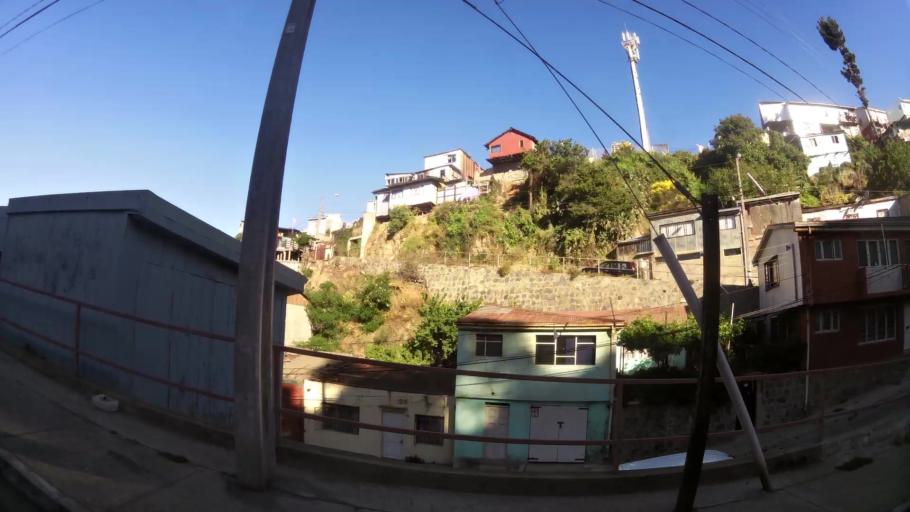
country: CL
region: Valparaiso
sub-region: Provincia de Valparaiso
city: Valparaiso
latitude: -33.0550
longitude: -71.6263
